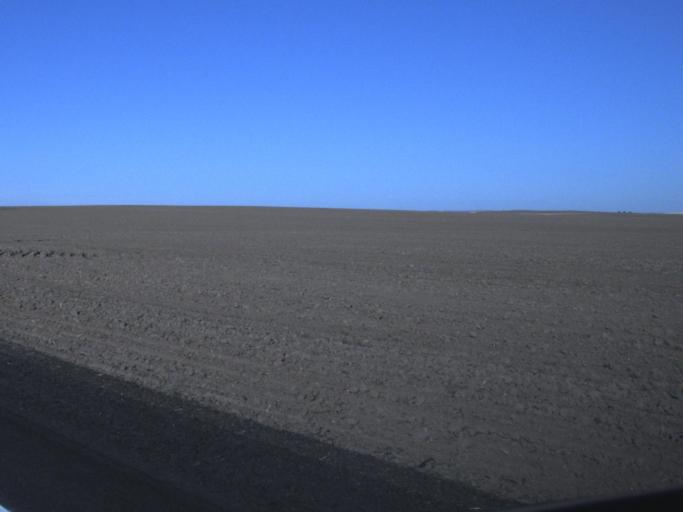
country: US
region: Washington
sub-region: Adams County
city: Ritzville
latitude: 46.9584
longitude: -118.3434
